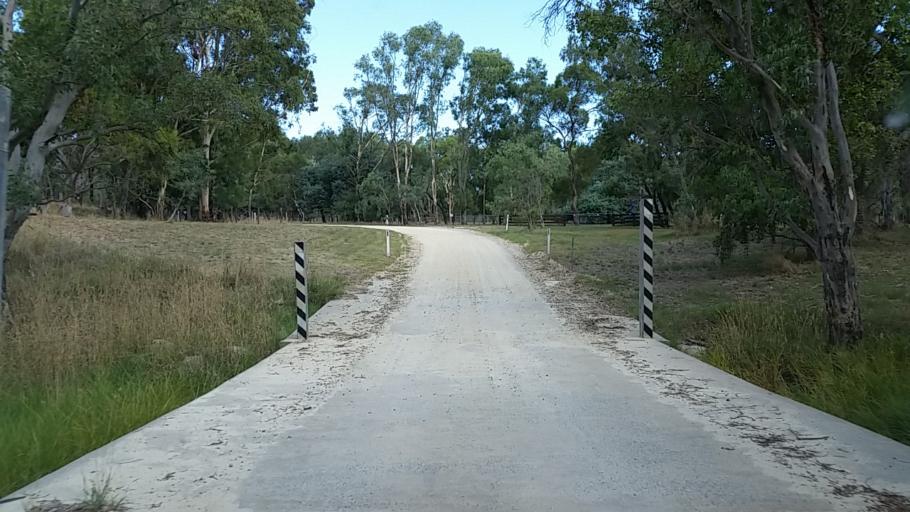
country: AU
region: South Australia
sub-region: Barossa
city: Angaston
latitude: -34.5650
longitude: 139.0813
